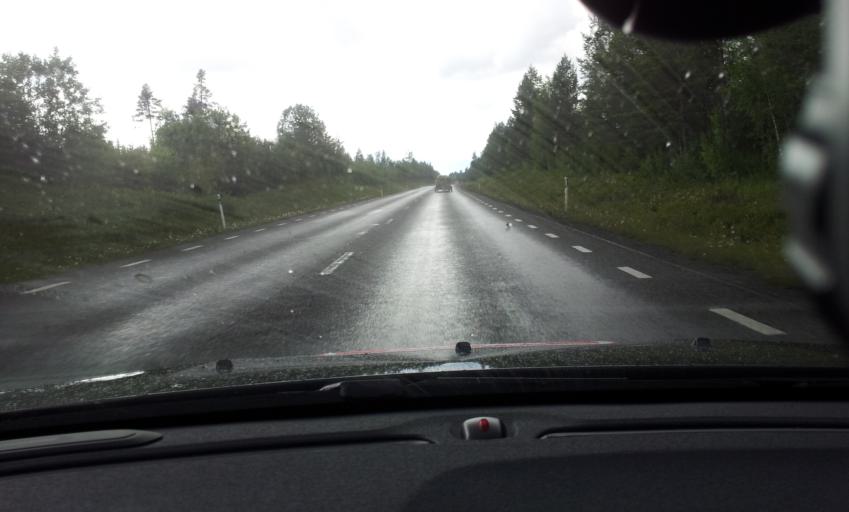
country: SE
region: Jaemtland
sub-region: Krokoms Kommun
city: Valla
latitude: 63.3074
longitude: 13.8193
